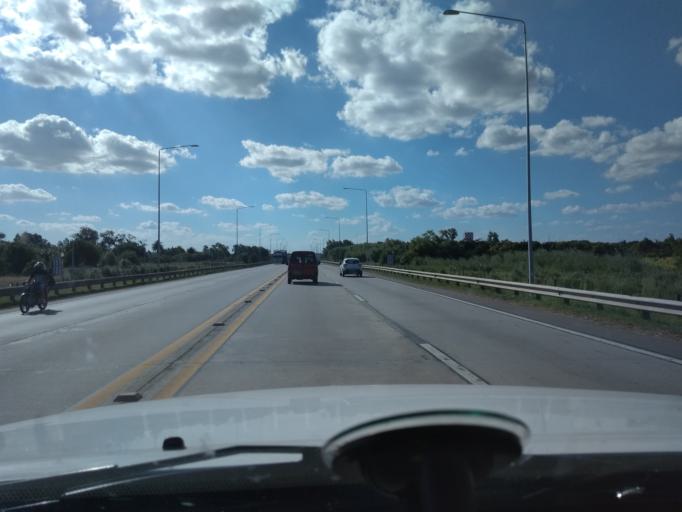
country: UY
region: Canelones
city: La Paz
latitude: -34.7784
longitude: -56.2610
